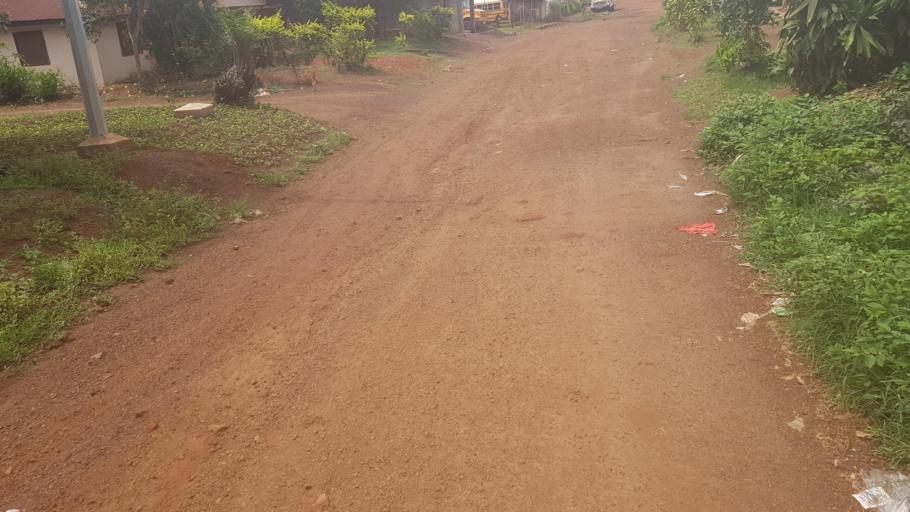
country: SL
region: Southern Province
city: Mogbwemo
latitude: 7.7583
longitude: -12.3051
